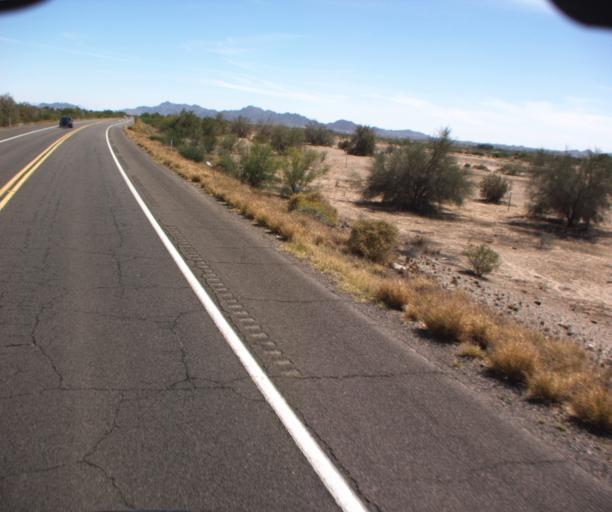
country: US
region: Arizona
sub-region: Pinal County
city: Sacaton
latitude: 33.1367
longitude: -111.7540
